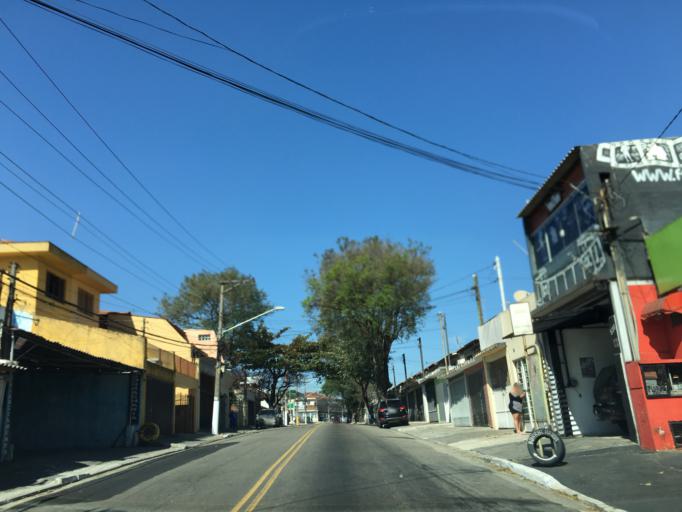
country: BR
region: Sao Paulo
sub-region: Taboao Da Serra
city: Taboao da Serra
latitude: -23.5800
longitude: -46.7610
